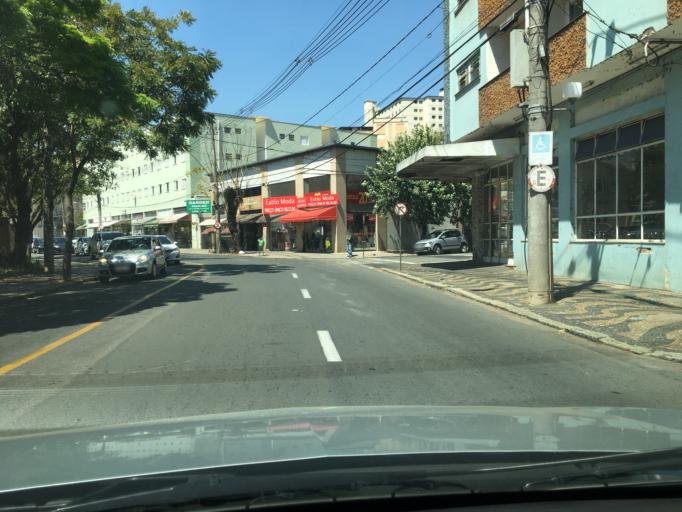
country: BR
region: Minas Gerais
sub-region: Pocos De Caldas
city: Pocos de Caldas
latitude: -21.7873
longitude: -46.5704
